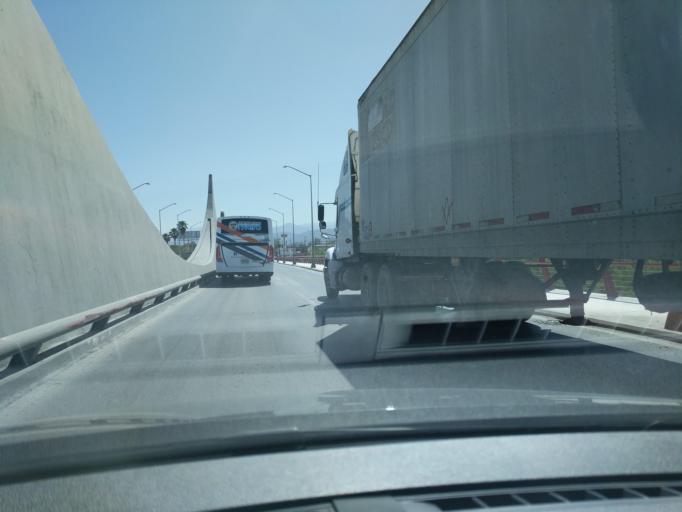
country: MX
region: Nuevo Leon
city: Juarez
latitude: 25.6465
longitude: -100.0851
